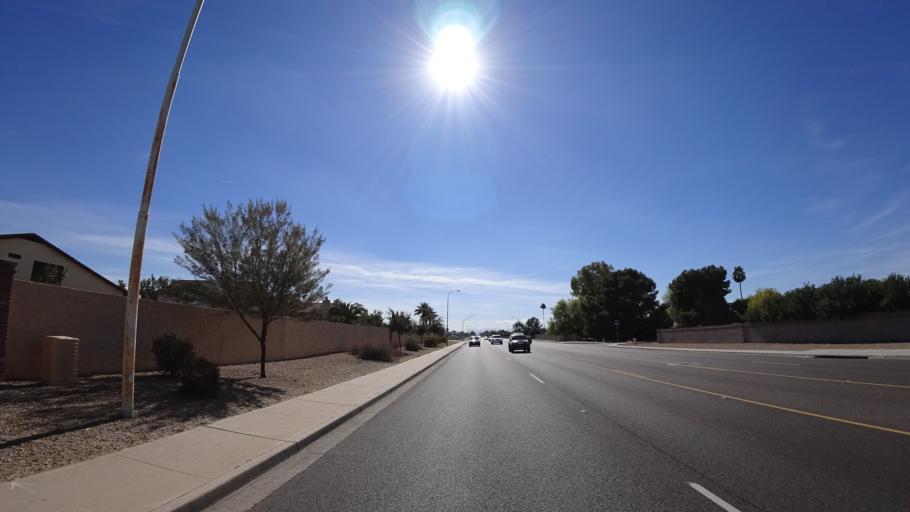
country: US
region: Arizona
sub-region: Maricopa County
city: Peoria
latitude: 33.6157
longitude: -112.2025
